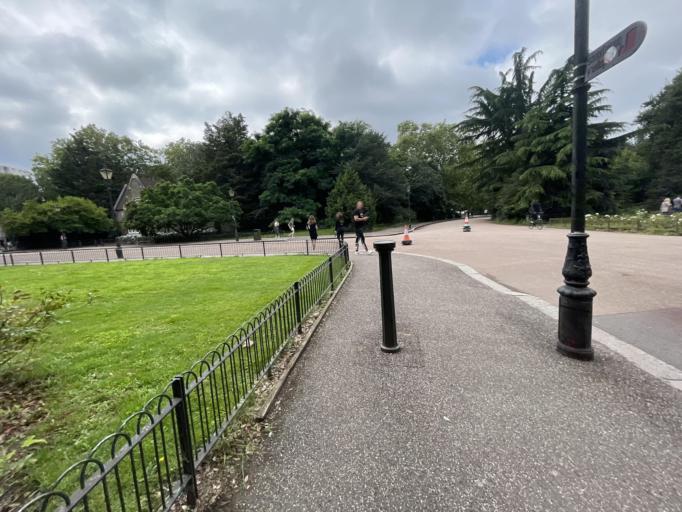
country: GB
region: England
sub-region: Greater London
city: Battersea
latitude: 51.4784
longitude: -0.1496
